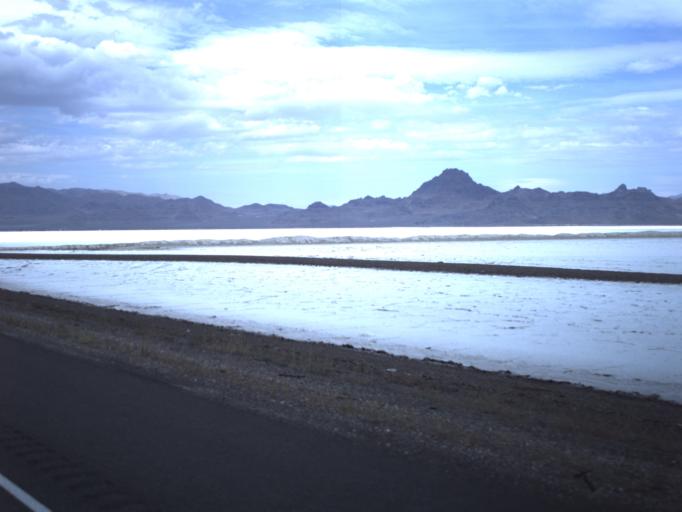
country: US
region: Utah
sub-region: Tooele County
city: Wendover
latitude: 40.7405
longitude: -113.9061
